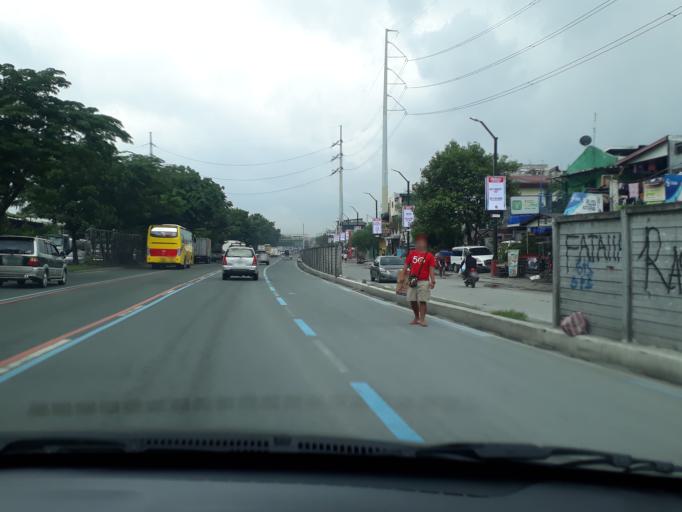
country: PH
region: Calabarzon
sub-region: Province of Rizal
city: Pateros
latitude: 14.5308
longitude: 121.0574
